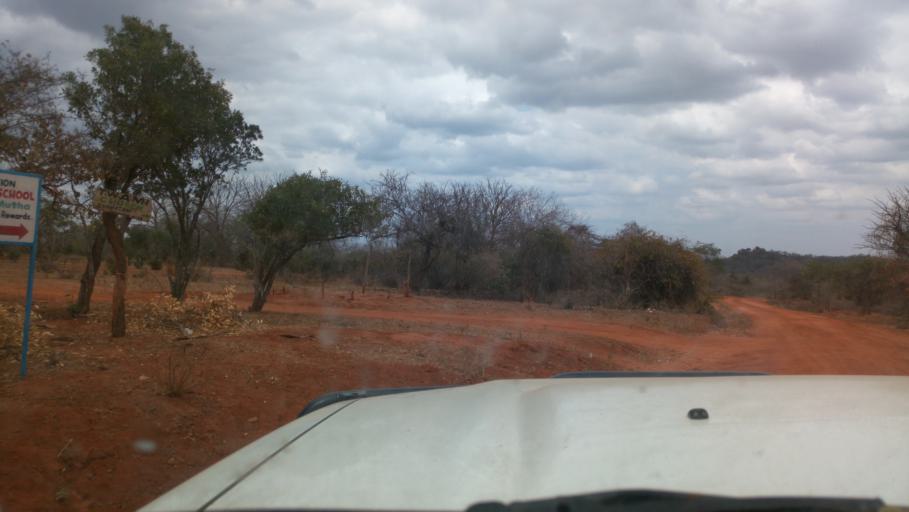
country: KE
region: Kitui
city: Kitui
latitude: -1.8910
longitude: 38.4172
